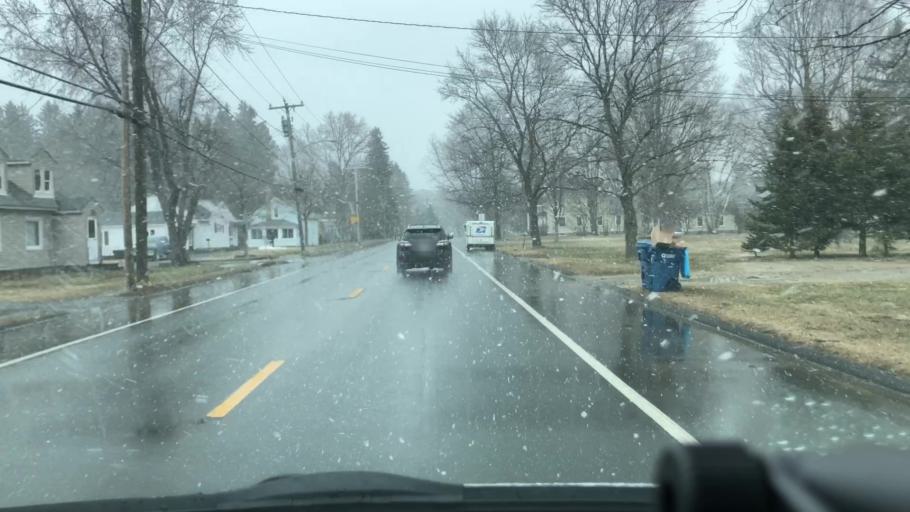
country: US
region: Massachusetts
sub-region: Berkshire County
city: Dalton
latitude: 42.4829
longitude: -73.1520
